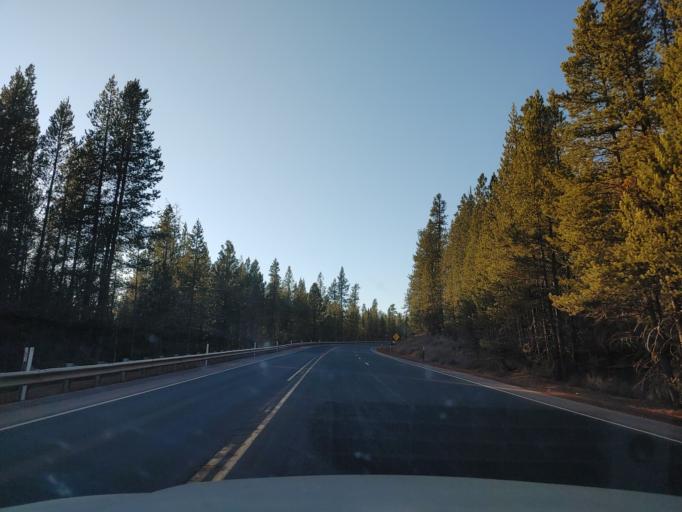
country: US
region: Oregon
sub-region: Deschutes County
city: La Pine
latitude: 43.4427
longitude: -121.8680
